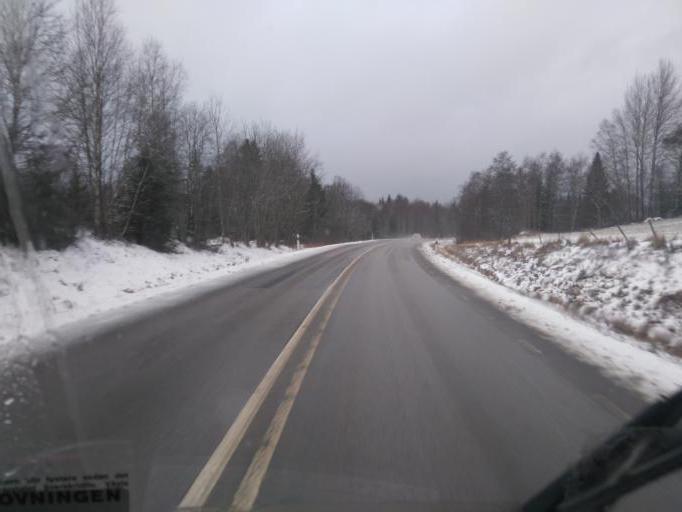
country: SE
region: Joenkoeping
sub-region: Eksjo Kommun
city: Mariannelund
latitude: 57.6333
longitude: 15.6372
